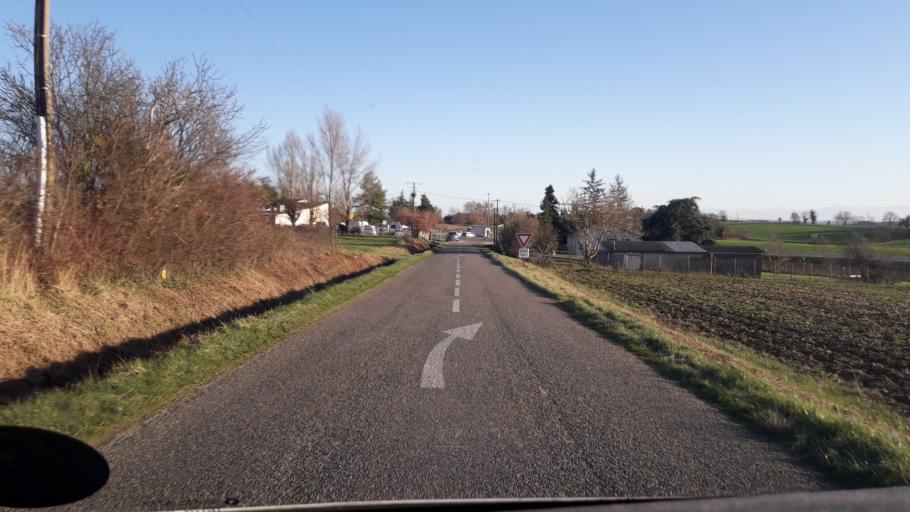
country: FR
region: Midi-Pyrenees
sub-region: Departement du Gers
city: Gimont
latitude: 43.6090
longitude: 0.9755
